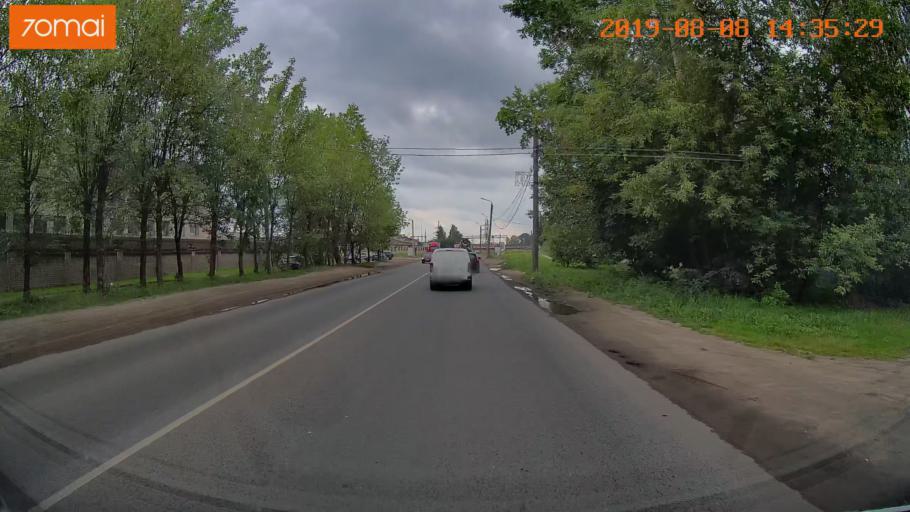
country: RU
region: Ivanovo
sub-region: Gorod Ivanovo
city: Ivanovo
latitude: 56.9745
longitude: 40.9544
